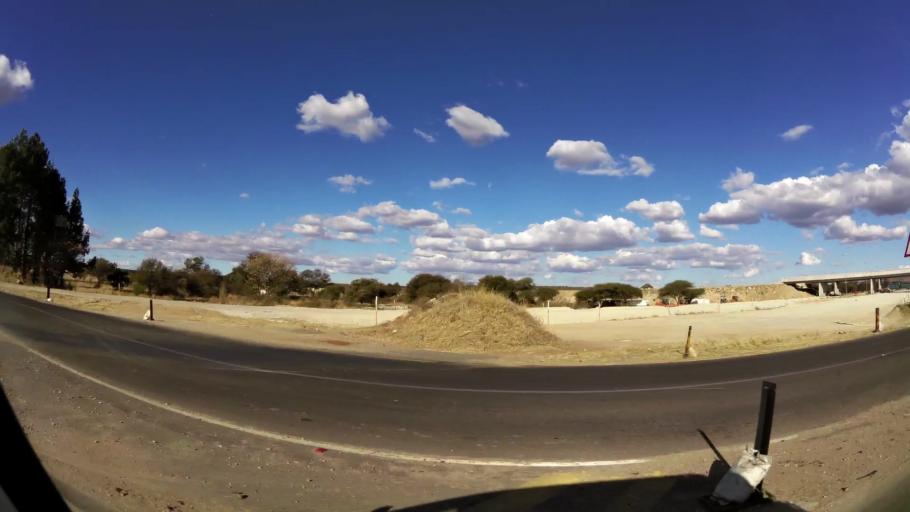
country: ZA
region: Limpopo
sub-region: Capricorn District Municipality
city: Polokwane
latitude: -23.9397
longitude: 29.4488
